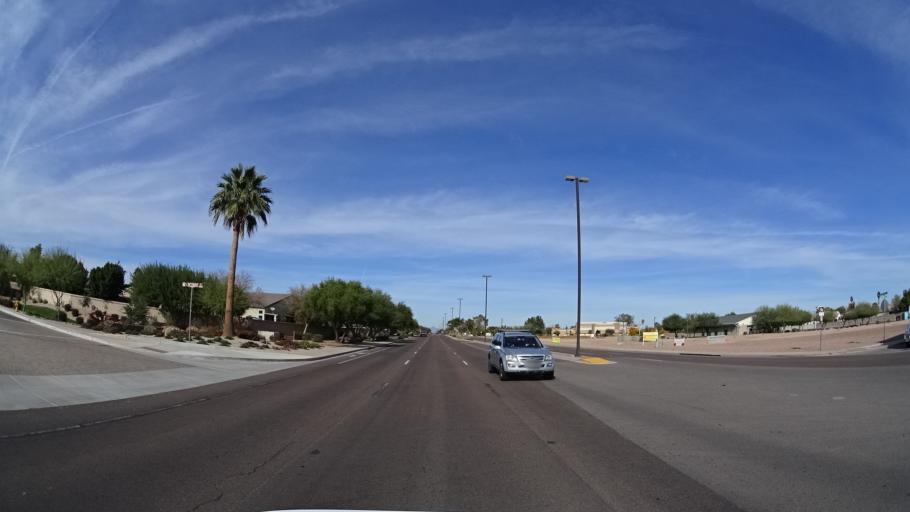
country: US
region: Arizona
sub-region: Maricopa County
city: Gilbert
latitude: 33.3084
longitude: -111.7899
